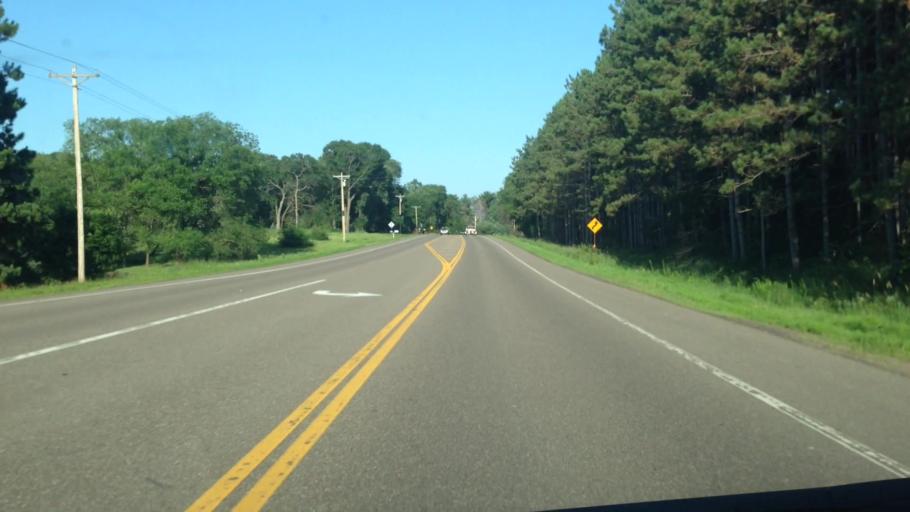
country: US
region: Minnesota
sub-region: Sherburne County
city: Zimmerman
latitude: 45.4448
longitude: -93.6284
